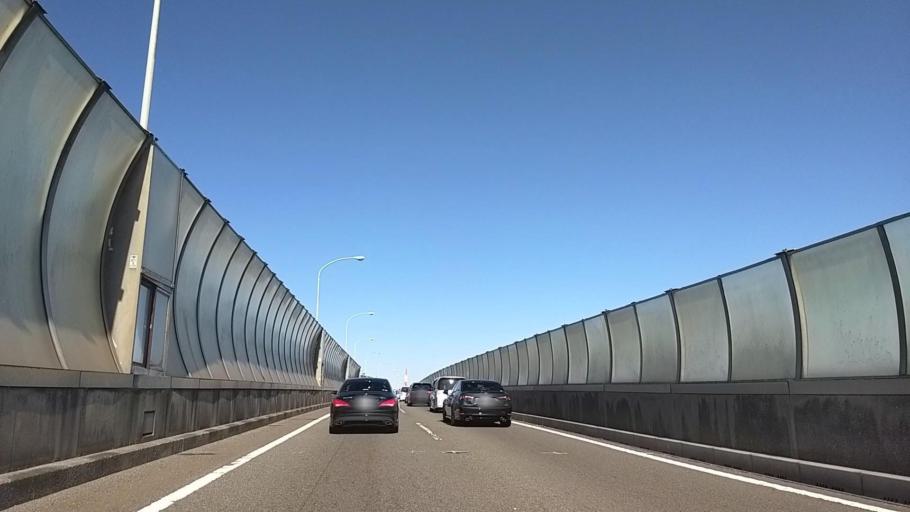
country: JP
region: Kanagawa
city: Minami-rinkan
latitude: 35.4971
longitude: 139.4940
